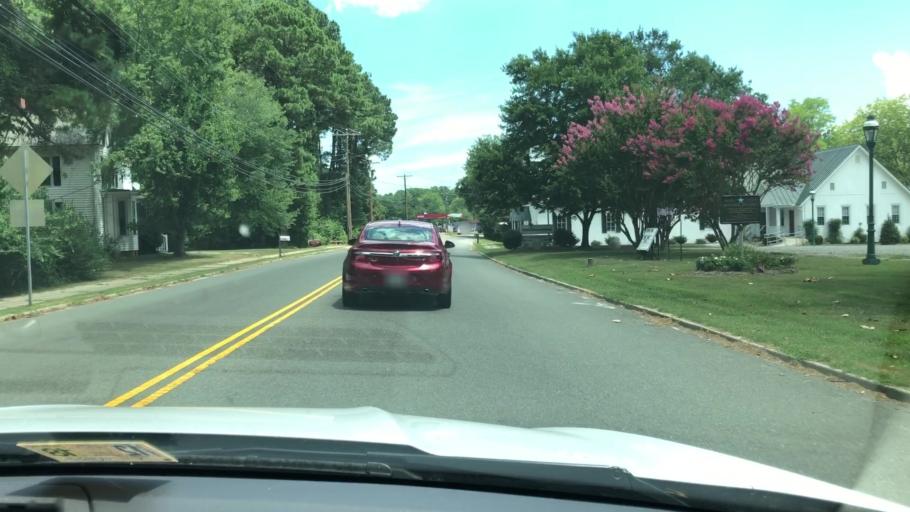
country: US
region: Virginia
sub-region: Lancaster County
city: Lancaster
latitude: 37.7696
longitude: -76.4632
